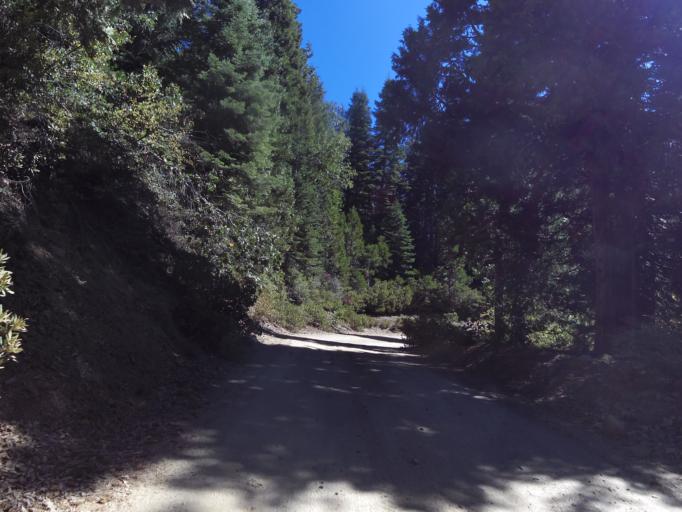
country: US
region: California
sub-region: Madera County
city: Oakhurst
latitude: 37.4456
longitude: -119.5244
